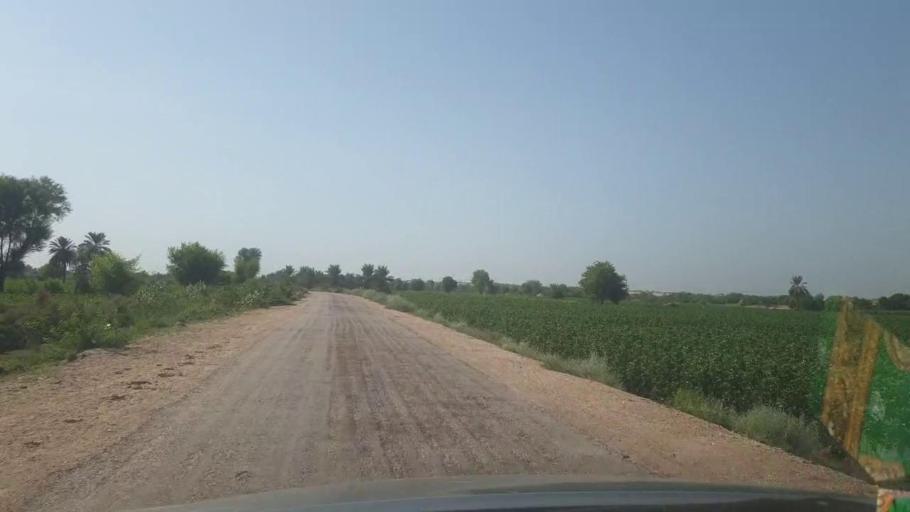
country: PK
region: Sindh
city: Rohri
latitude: 27.4670
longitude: 69.0376
